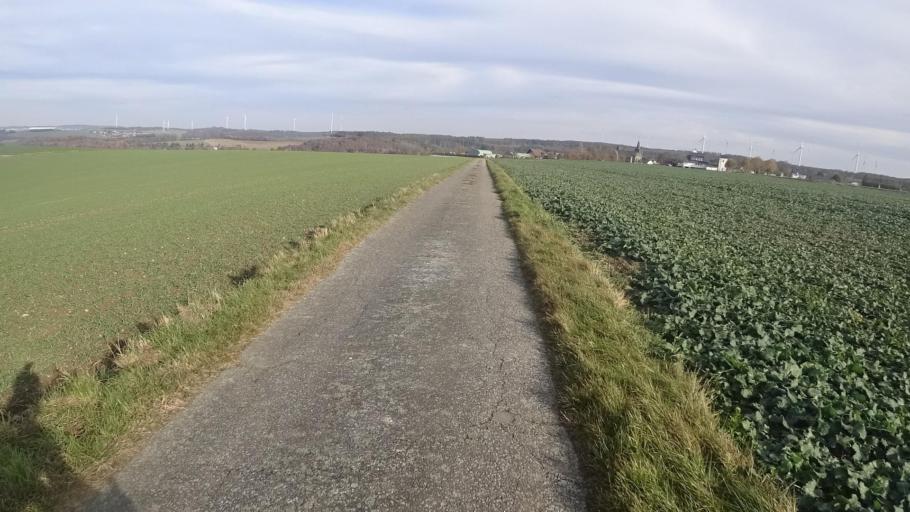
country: DE
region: Rheinland-Pfalz
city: Lingerhahn
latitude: 50.0942
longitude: 7.5553
